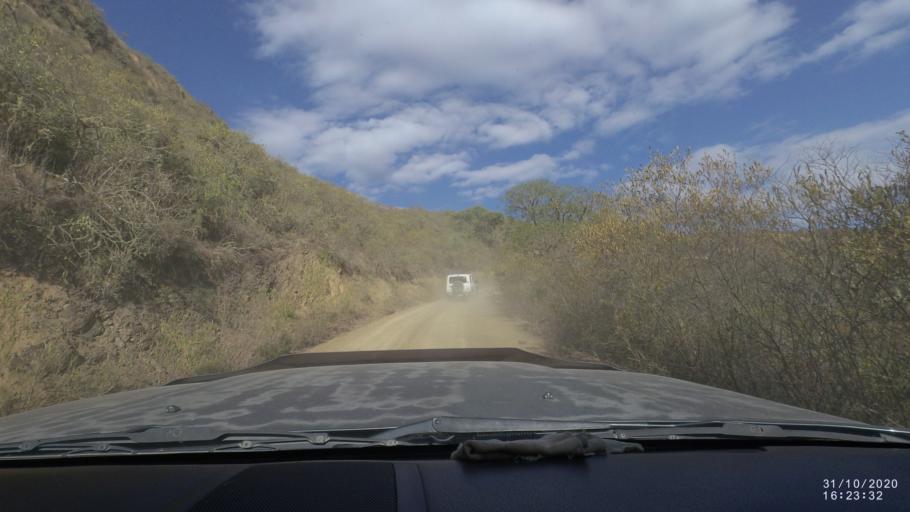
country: BO
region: Chuquisaca
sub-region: Provincia Zudanez
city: Mojocoya
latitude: -18.3989
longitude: -64.5901
